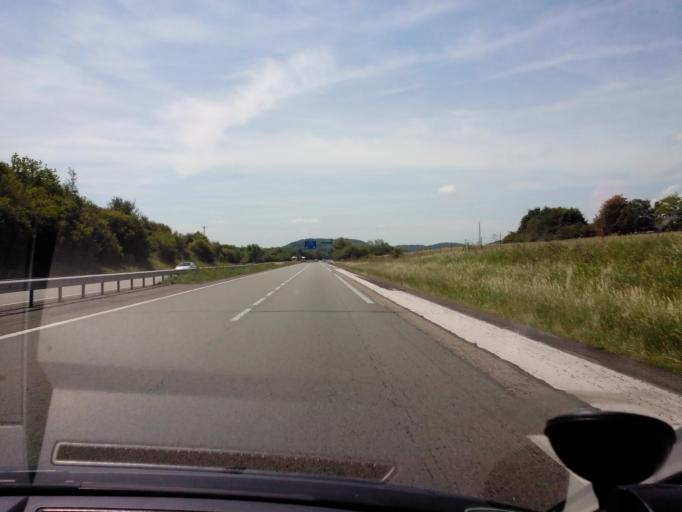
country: FR
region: Champagne-Ardenne
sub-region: Departement de la Haute-Marne
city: Avrecourt
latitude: 47.9992
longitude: 5.5148
